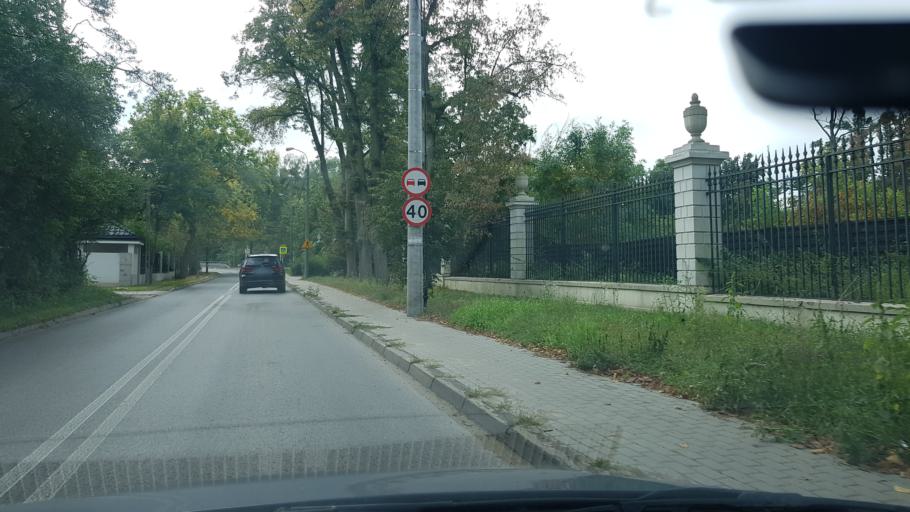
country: PL
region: Masovian Voivodeship
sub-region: Powiat piaseczynski
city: Konstancin-Jeziorna
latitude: 52.0840
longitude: 21.0946
